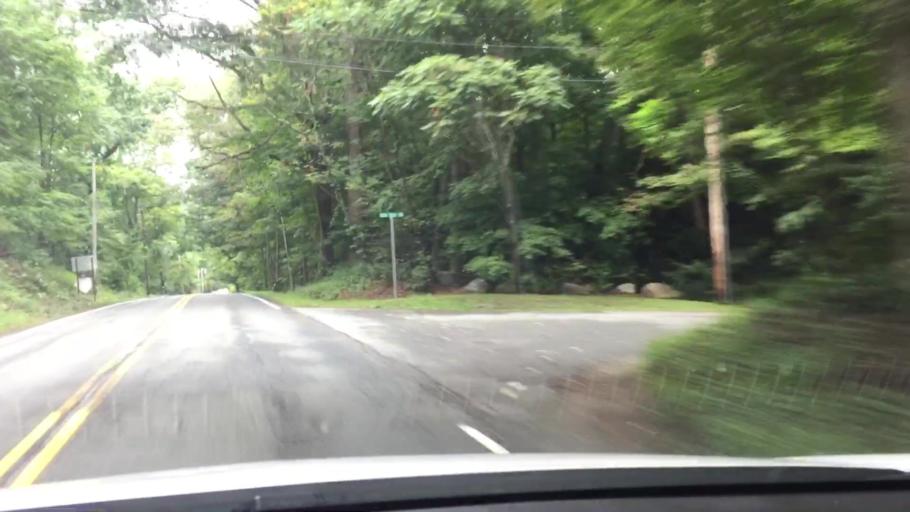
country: US
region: Massachusetts
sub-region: Berkshire County
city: Housatonic
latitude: 42.2357
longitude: -73.3703
